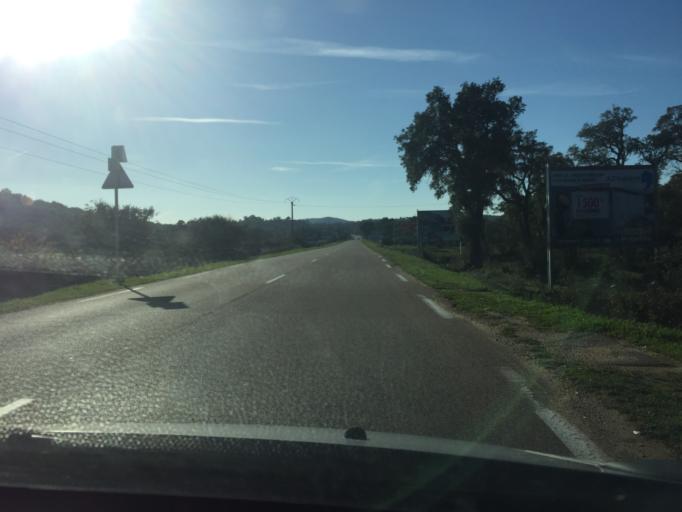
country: FR
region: Corsica
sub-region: Departement de la Corse-du-Sud
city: Porto-Vecchio
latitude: 41.6440
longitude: 9.2958
